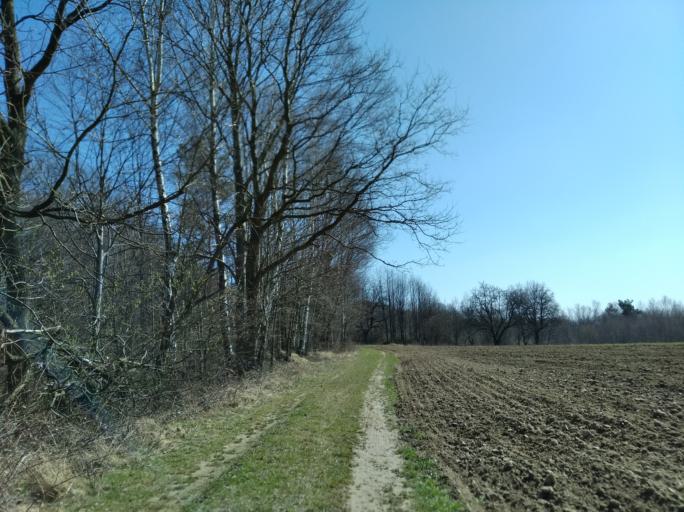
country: PL
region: Subcarpathian Voivodeship
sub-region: Powiat strzyzowski
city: Strzyzow
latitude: 49.8525
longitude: 21.8174
